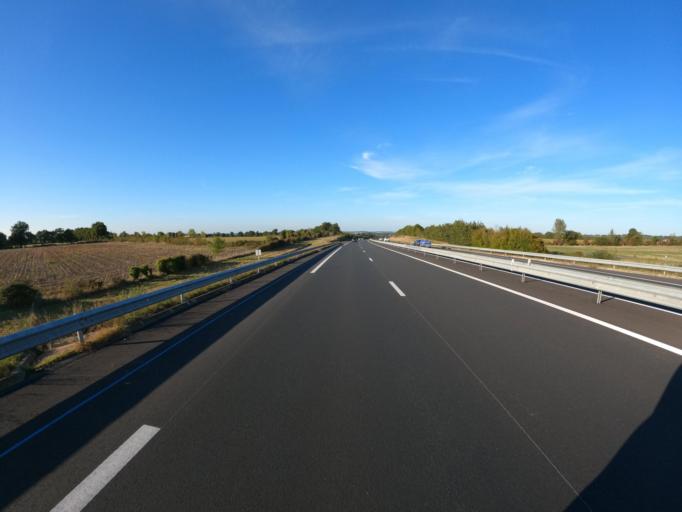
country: FR
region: Pays de la Loire
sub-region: Departement de la Vendee
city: Mortagne-sur-Sevre
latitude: 46.9821
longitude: -0.9180
